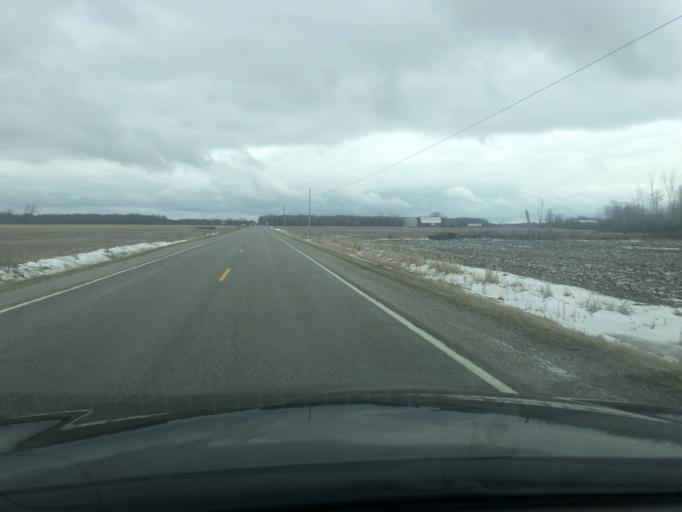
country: US
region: Michigan
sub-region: Saint Clair County
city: Saint Clair
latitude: 42.8212
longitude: -82.5551
